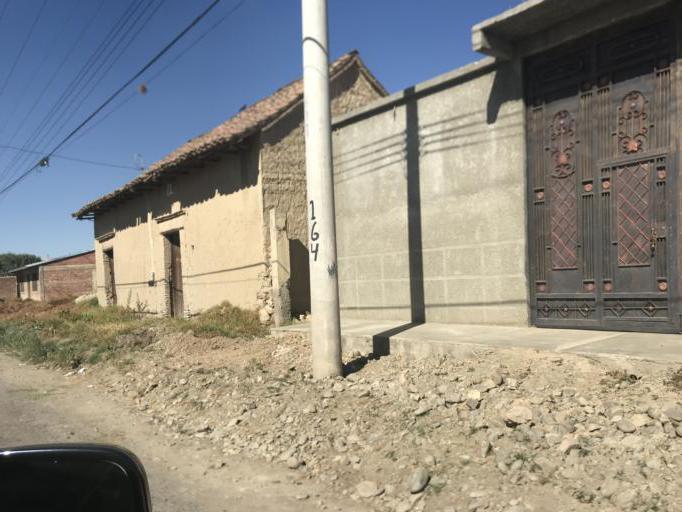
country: BO
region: Cochabamba
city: Cliza
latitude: -17.5646
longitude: -65.8859
